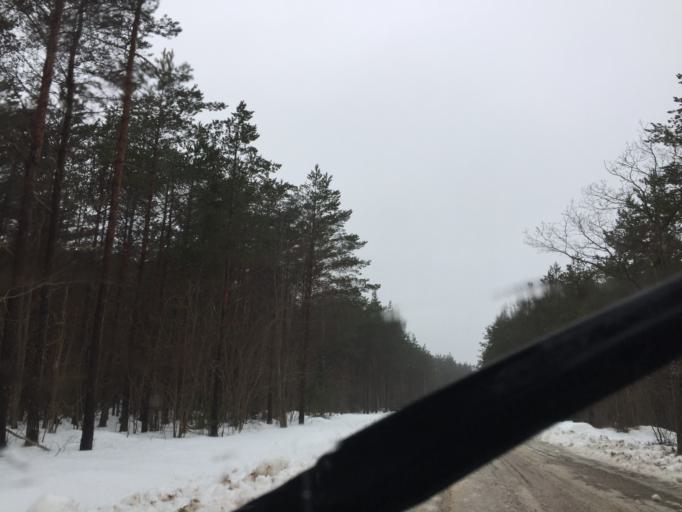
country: EE
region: Saare
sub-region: Kuressaare linn
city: Kuressaare
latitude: 58.2951
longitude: 22.1015
